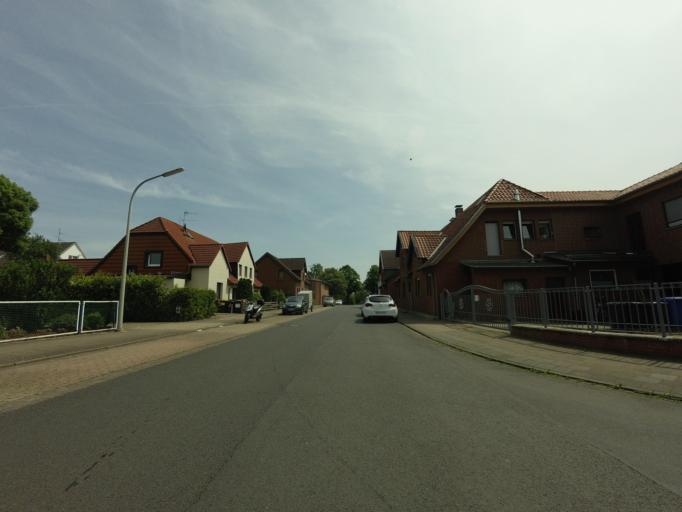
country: DE
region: Lower Saxony
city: Braunschweig
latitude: 52.3074
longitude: 10.4891
